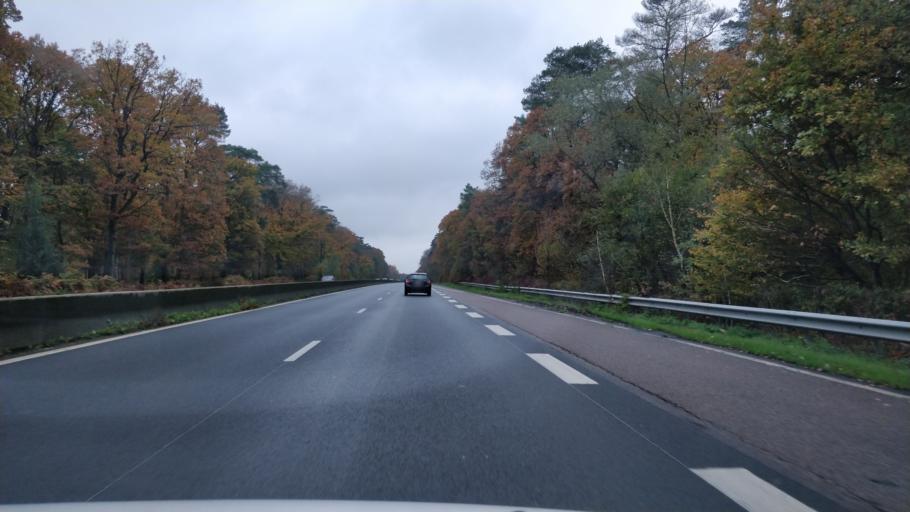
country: FR
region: Haute-Normandie
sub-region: Departement de la Seine-Maritime
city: Grand-Couronne
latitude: 49.3435
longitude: 1.0076
